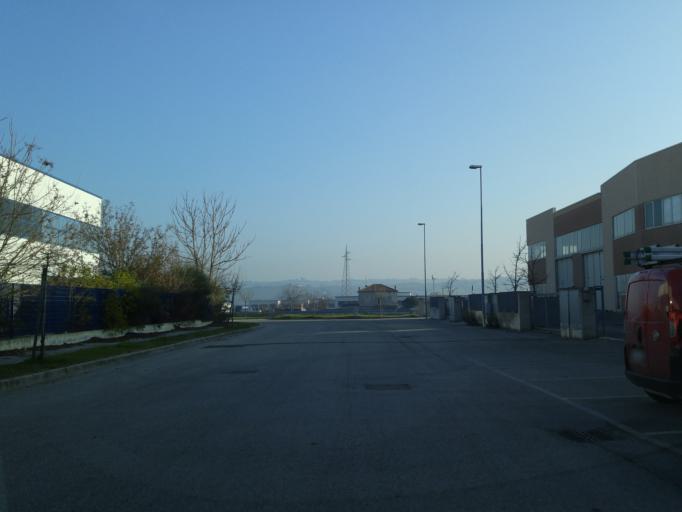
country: IT
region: The Marches
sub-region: Provincia di Pesaro e Urbino
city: Lucrezia
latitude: 43.7698
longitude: 12.9548
